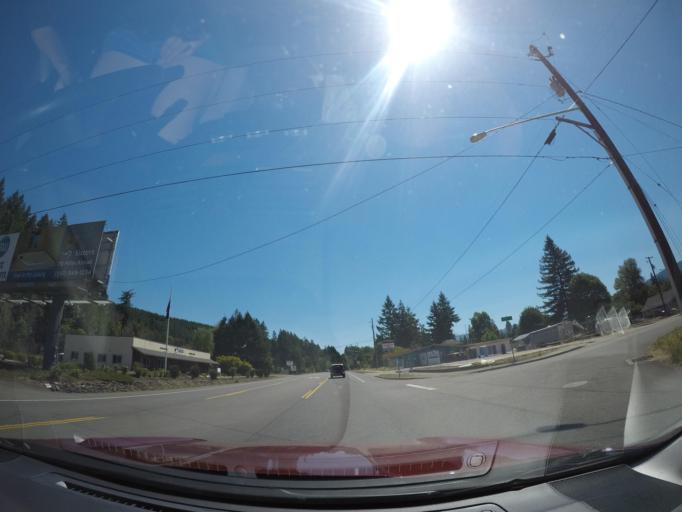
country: US
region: Oregon
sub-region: Linn County
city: Mill City
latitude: 44.7573
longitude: -122.4878
